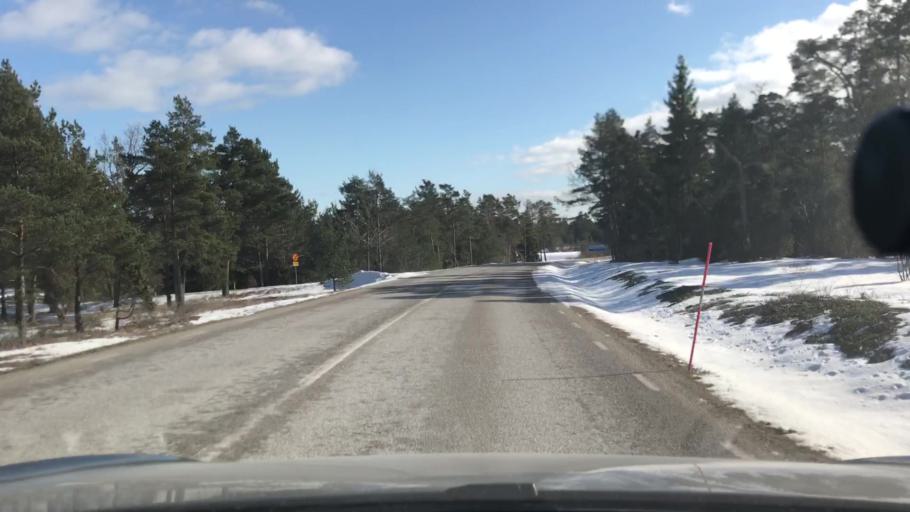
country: SE
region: Gotland
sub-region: Gotland
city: Hemse
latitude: 57.3466
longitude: 18.6923
